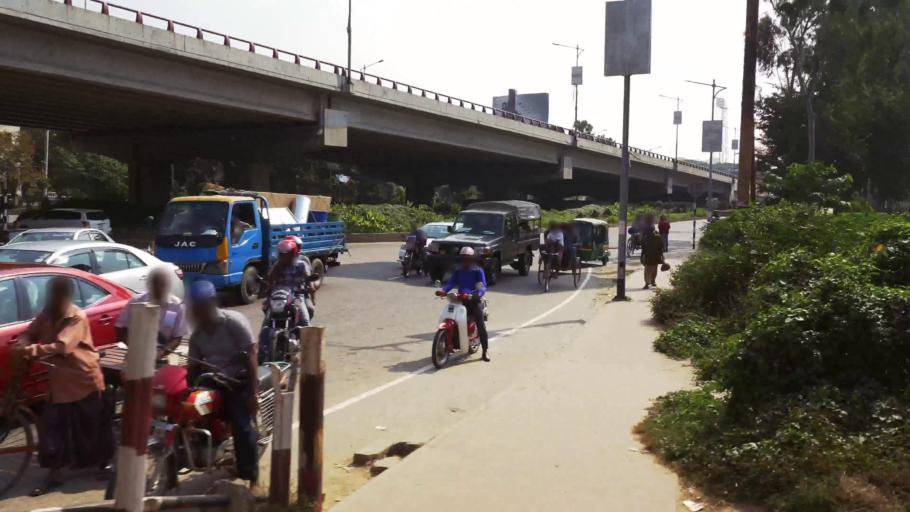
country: BD
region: Dhaka
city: Tungi
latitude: 23.8424
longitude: 90.4163
